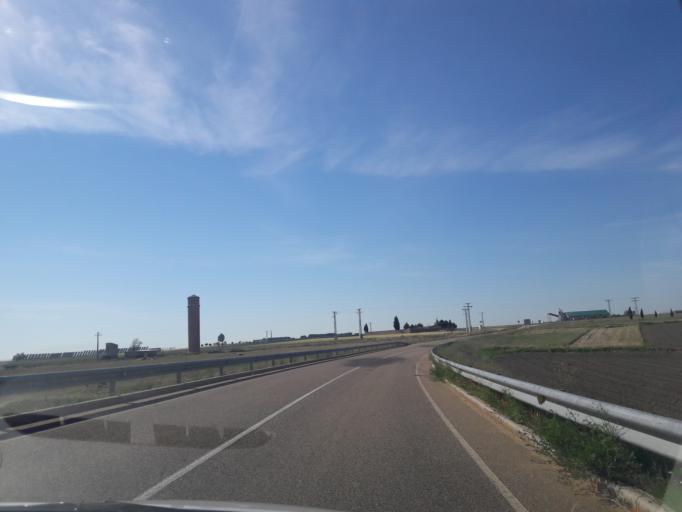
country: ES
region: Castille and Leon
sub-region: Provincia de Salamanca
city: Espino de la Orbada
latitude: 41.0825
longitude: -5.3952
